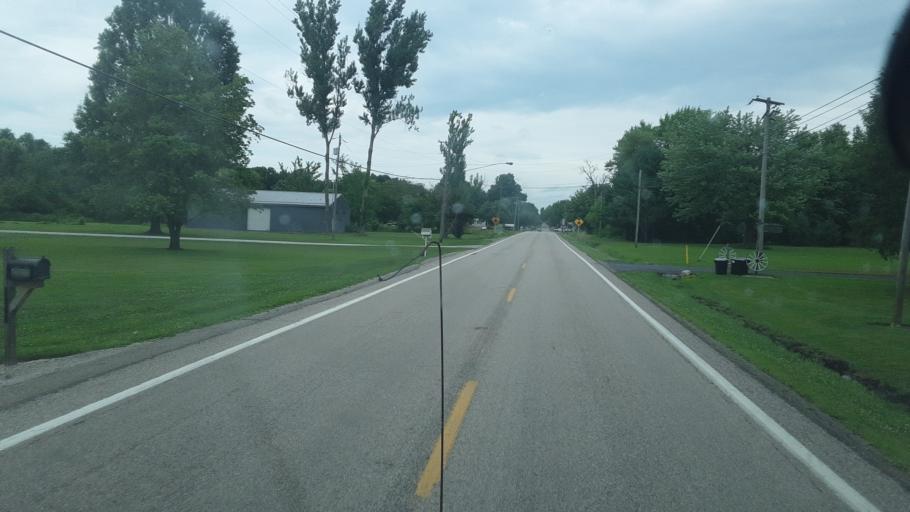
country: US
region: Ohio
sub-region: Trumbull County
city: Cortland
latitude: 41.3851
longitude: -80.6655
